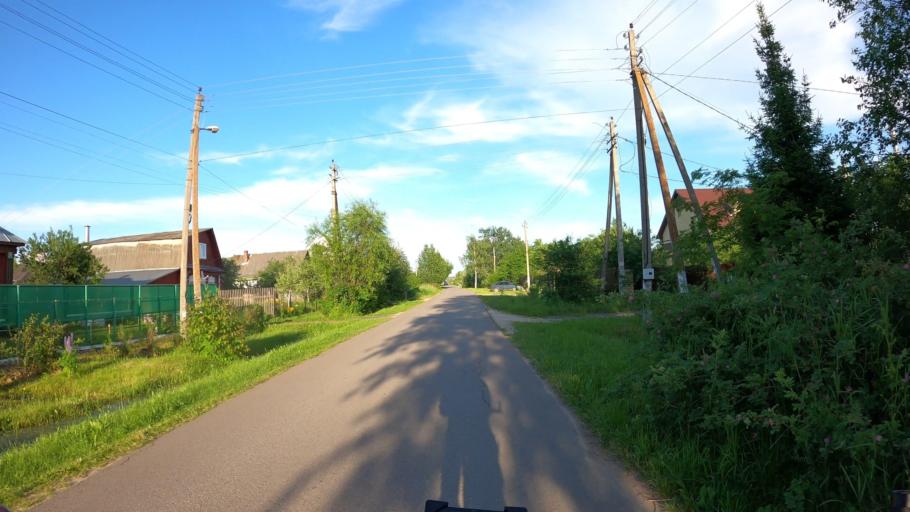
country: RU
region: Moskovskaya
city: Ashitkovo
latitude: 55.4562
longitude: 38.5811
